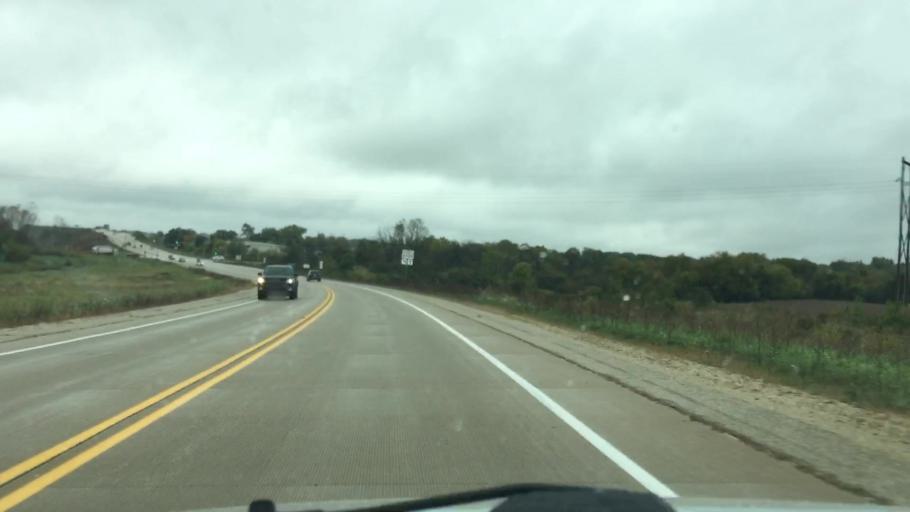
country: US
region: Wisconsin
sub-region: Walworth County
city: Whitewater
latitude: 42.8193
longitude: -88.7408
